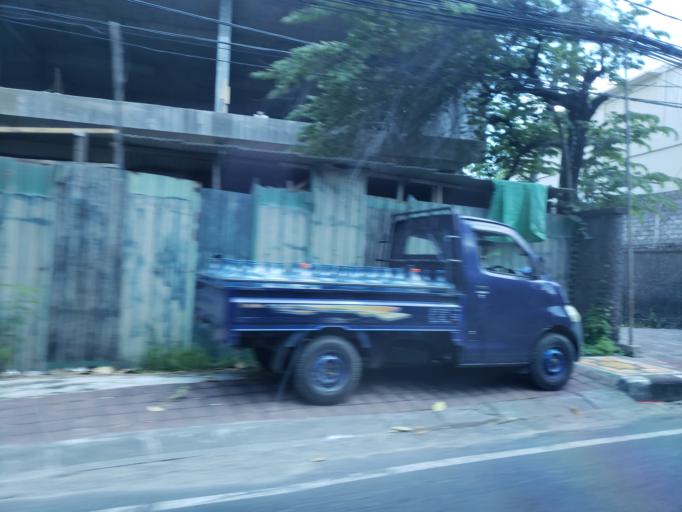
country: ID
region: Bali
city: Jimbaran
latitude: -8.7817
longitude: 115.1674
